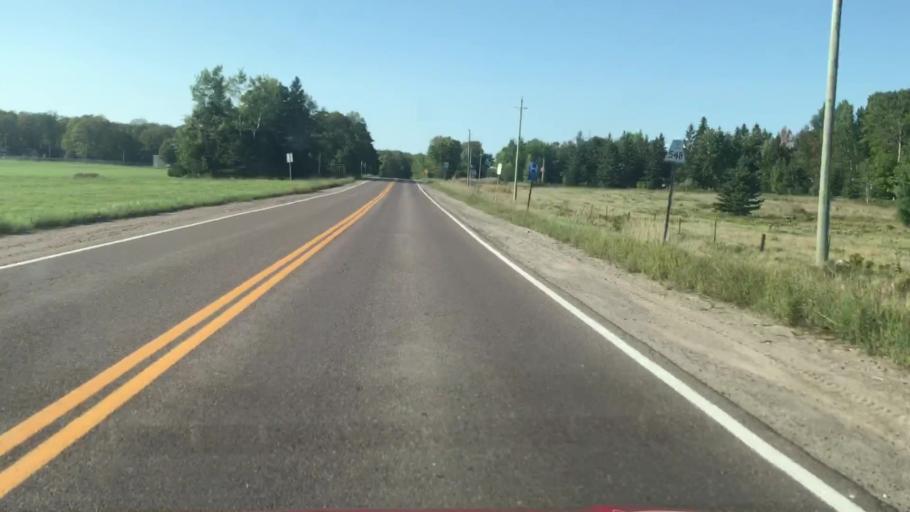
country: US
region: Michigan
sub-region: Chippewa County
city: Sault Ste. Marie
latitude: 46.2766
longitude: -84.0283
